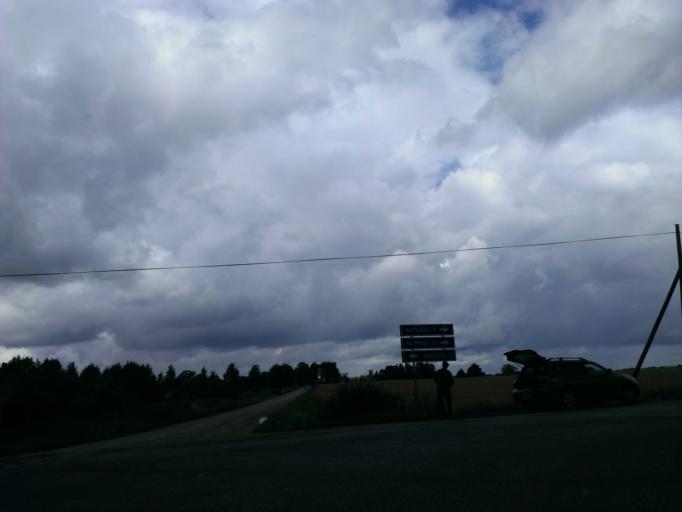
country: LV
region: Sigulda
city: Sigulda
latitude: 57.1599
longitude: 24.8992
